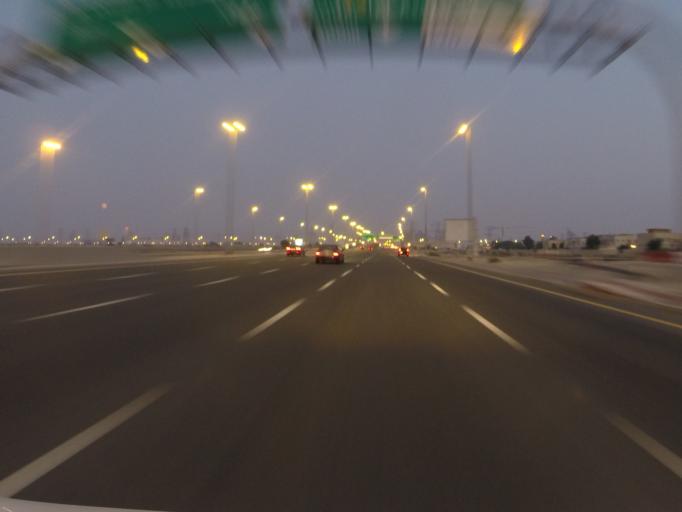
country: AE
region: Dubai
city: Dubai
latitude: 25.0721
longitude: 55.1878
